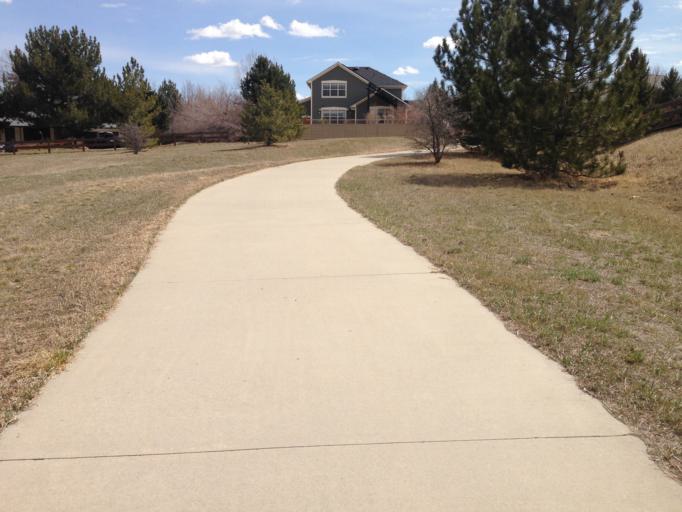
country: US
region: Colorado
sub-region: Boulder County
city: Louisville
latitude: 40.0076
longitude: -105.1411
